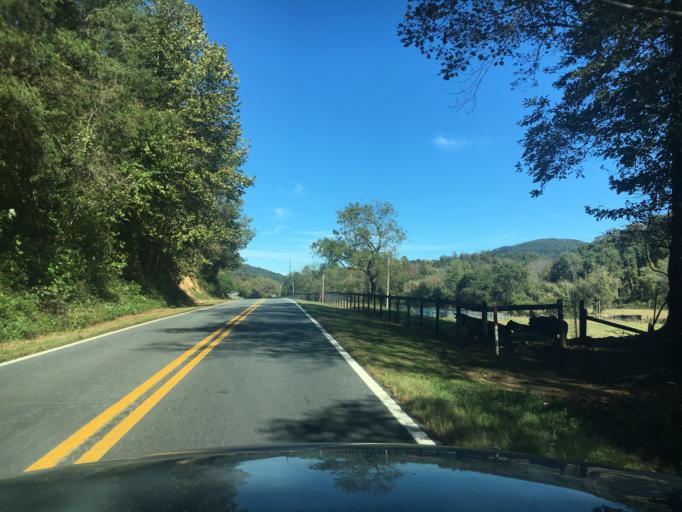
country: US
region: North Carolina
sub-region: Rutherford County
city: Spindale
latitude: 35.5238
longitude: -81.8552
